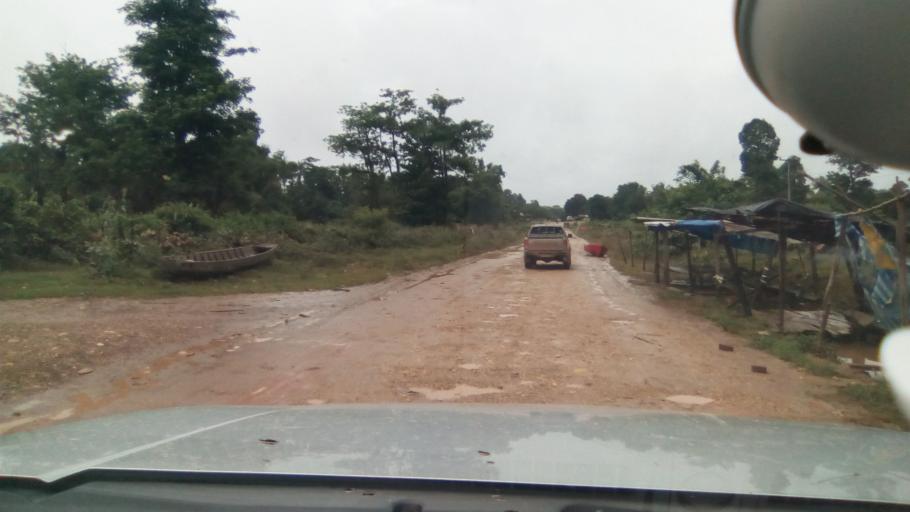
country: LA
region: Attapu
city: Attapu
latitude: 14.6784
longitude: 106.5798
